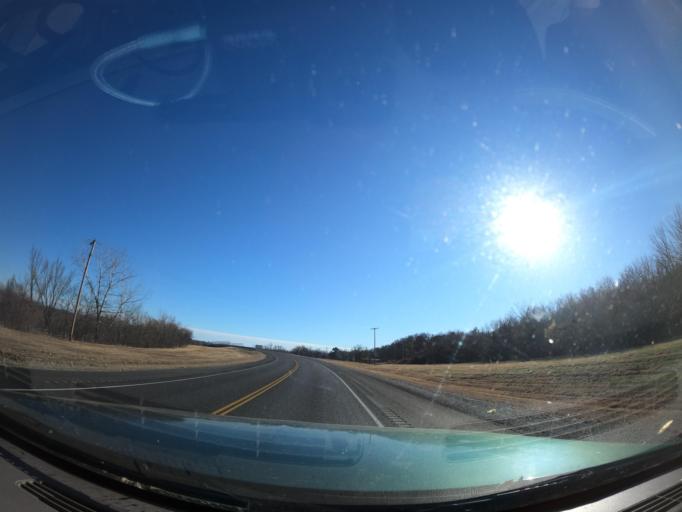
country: US
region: Oklahoma
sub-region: McIntosh County
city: Eufaula
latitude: 35.2708
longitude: -95.5853
